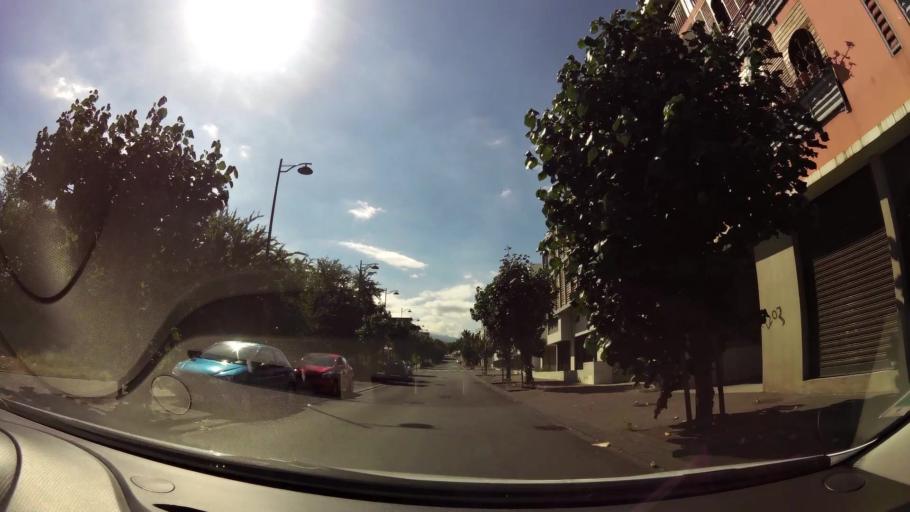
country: RE
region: Reunion
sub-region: Reunion
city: Saint-Pierre
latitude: -21.3389
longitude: 55.4636
